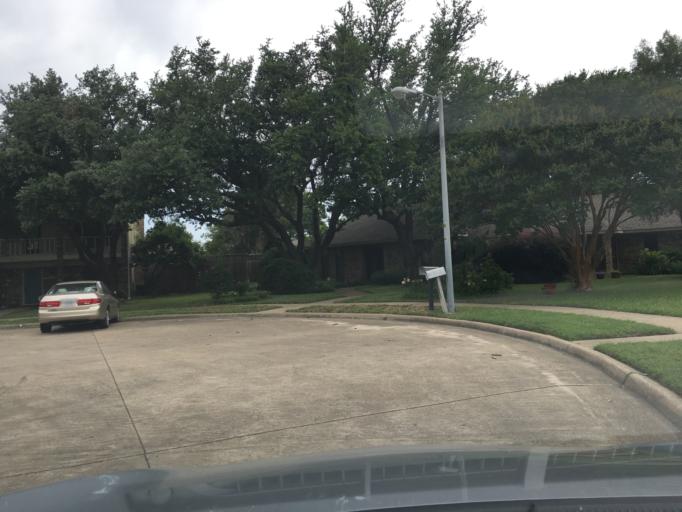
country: US
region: Texas
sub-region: Dallas County
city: Richardson
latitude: 32.9441
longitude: -96.7103
